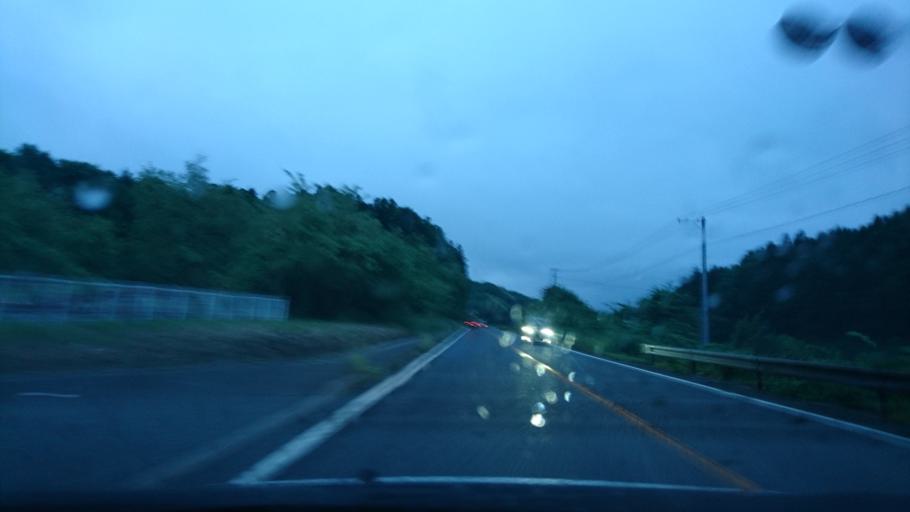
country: JP
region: Iwate
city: Ichinoseki
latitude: 38.7884
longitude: 141.0505
